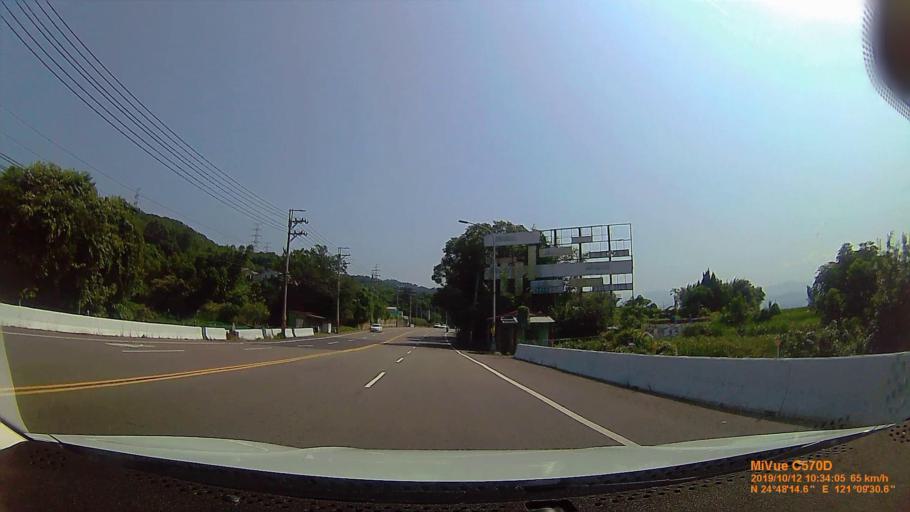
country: TW
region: Taiwan
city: Daxi
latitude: 24.8041
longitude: 121.1585
